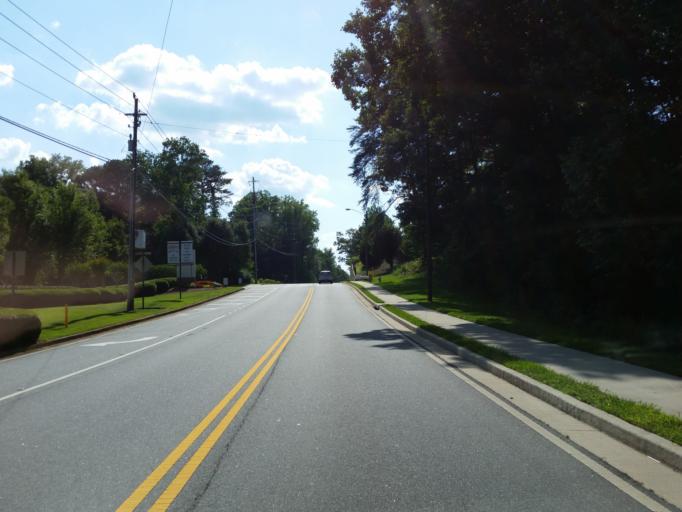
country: US
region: Georgia
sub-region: Cobb County
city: Marietta
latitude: 33.9833
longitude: -84.5026
